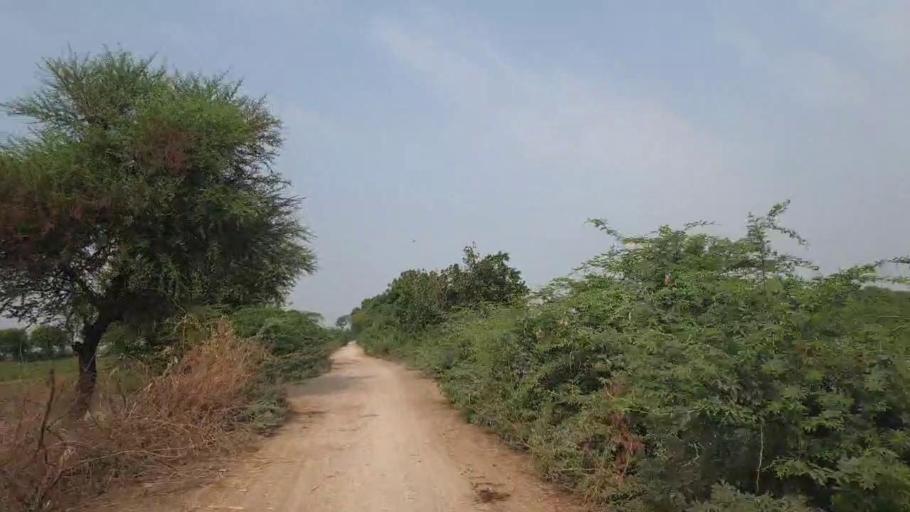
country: PK
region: Sindh
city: Badin
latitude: 24.5953
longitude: 68.7413
